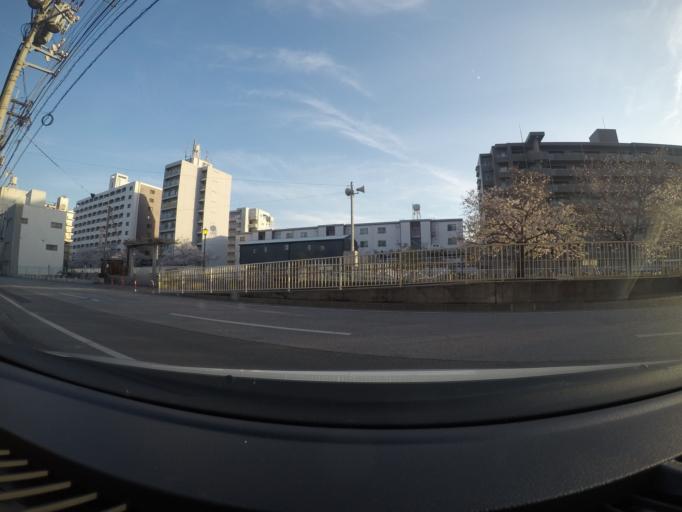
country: JP
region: Kochi
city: Kochi-shi
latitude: 33.5567
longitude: 133.5524
